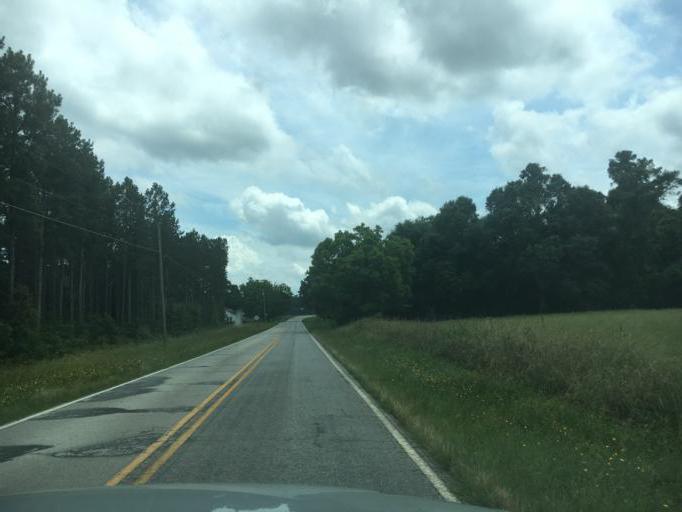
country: US
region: Georgia
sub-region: Hart County
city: Reed Creek
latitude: 34.4275
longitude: -82.9516
